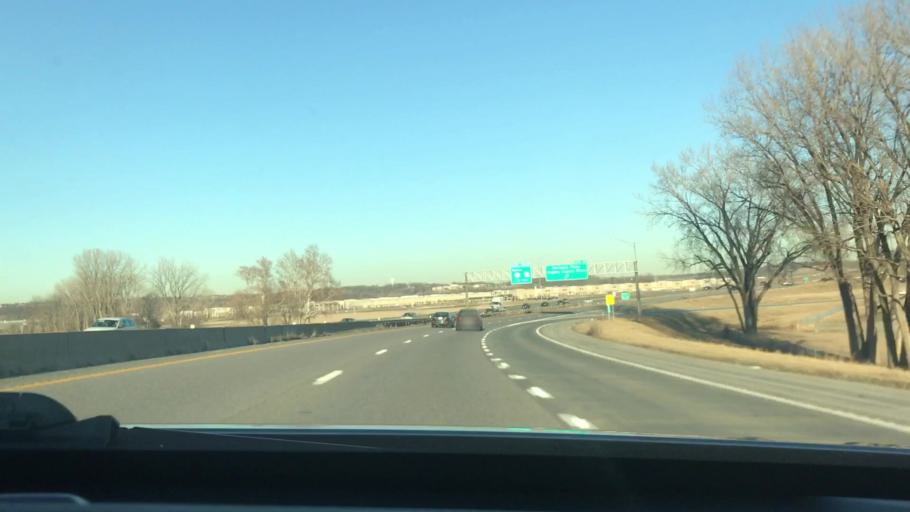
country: US
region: Missouri
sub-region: Platte County
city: Riverside
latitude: 39.1571
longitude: -94.6480
